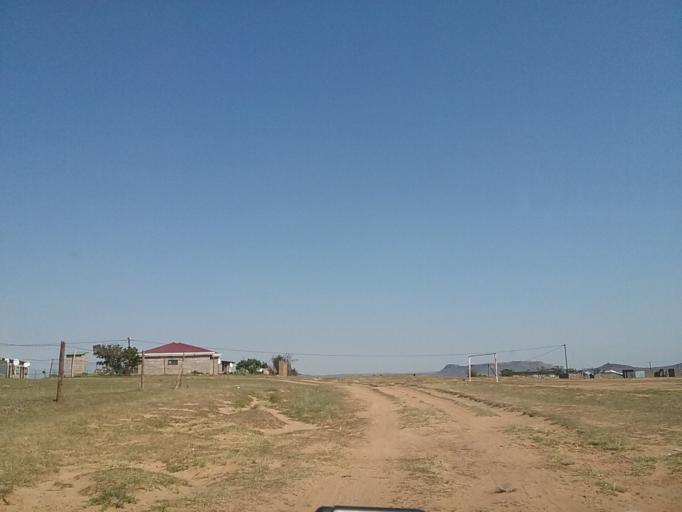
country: LS
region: Berea
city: Teyateyaneng
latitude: -29.1294
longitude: 27.7607
